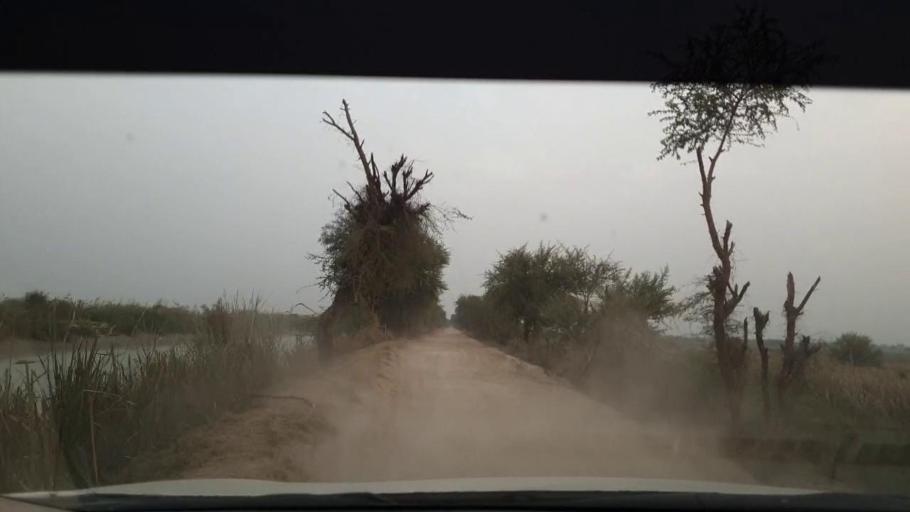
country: PK
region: Sindh
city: Berani
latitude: 25.8695
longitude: 68.7698
